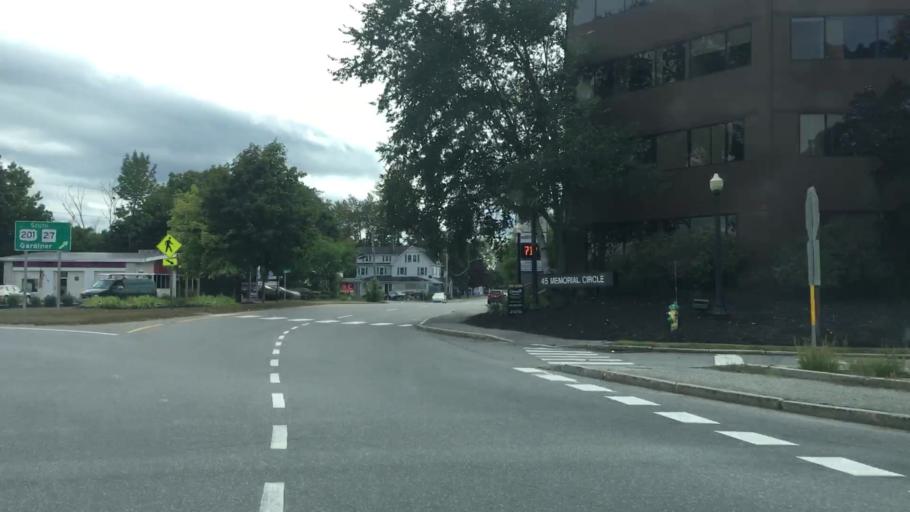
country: US
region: Maine
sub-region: Kennebec County
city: Augusta
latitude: 44.3105
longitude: -69.7798
